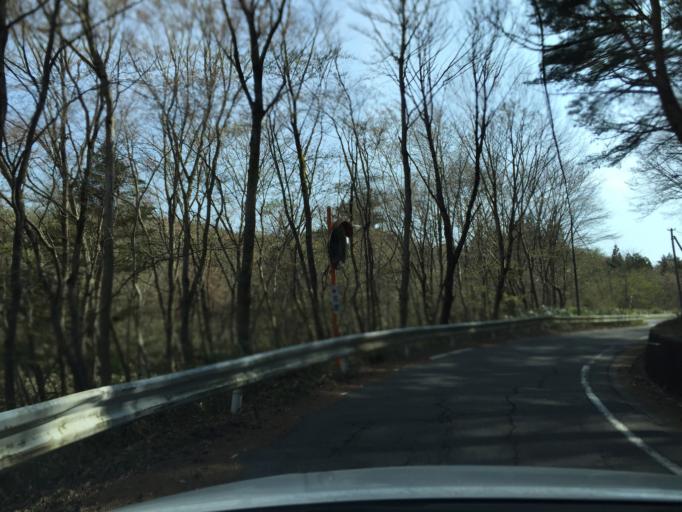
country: JP
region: Fukushima
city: Iwaki
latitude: 37.2181
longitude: 140.8511
